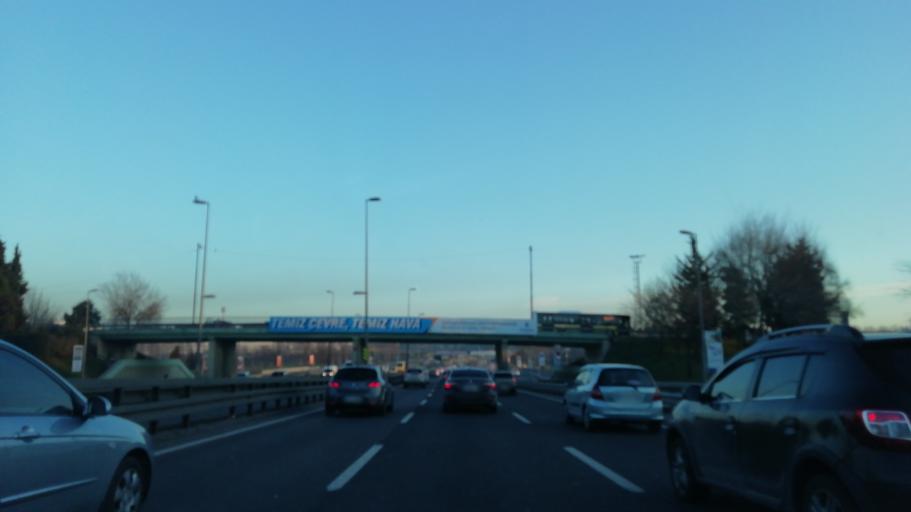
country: TR
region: Istanbul
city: Istanbul
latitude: 41.0271
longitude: 28.9235
